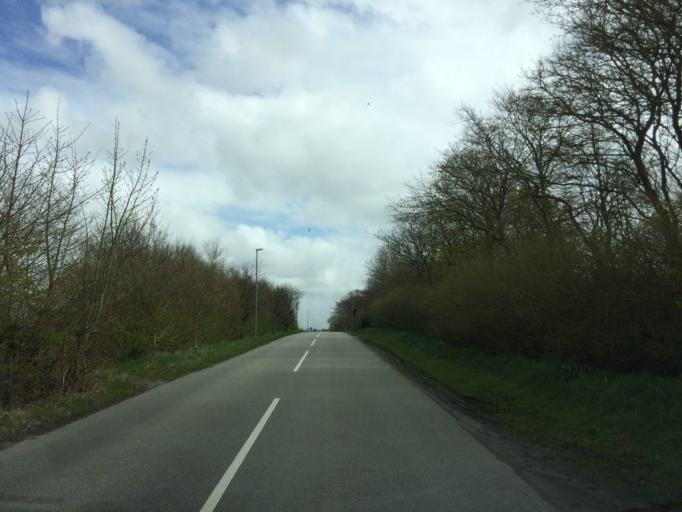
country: DK
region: South Denmark
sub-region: Varde Kommune
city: Oksbol
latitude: 55.5410
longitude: 8.3363
